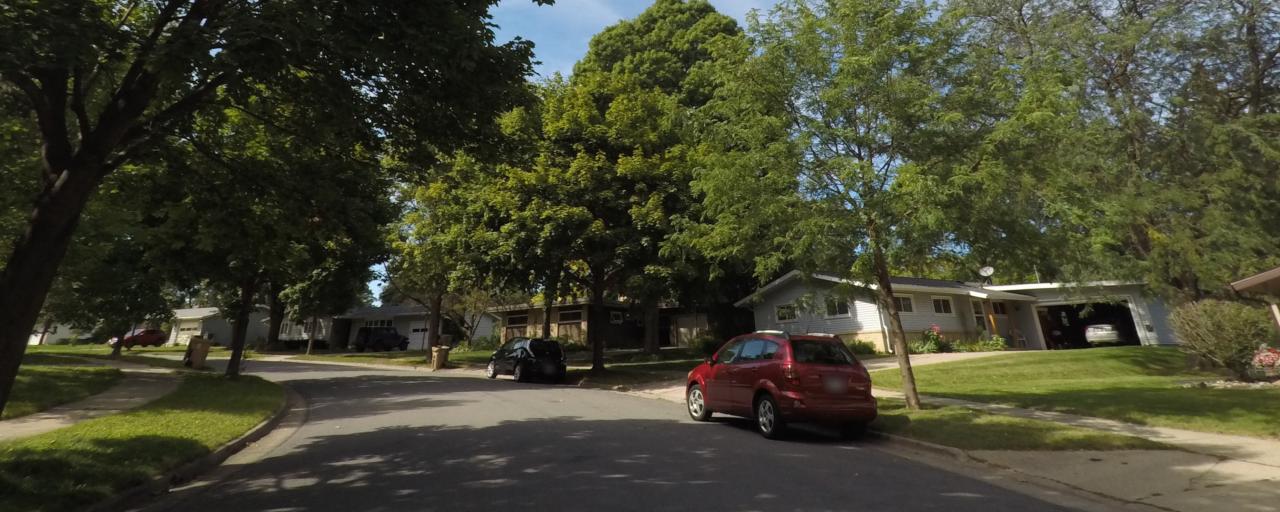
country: US
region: Wisconsin
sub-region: Dane County
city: Shorewood Hills
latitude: 43.0641
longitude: -89.4659
